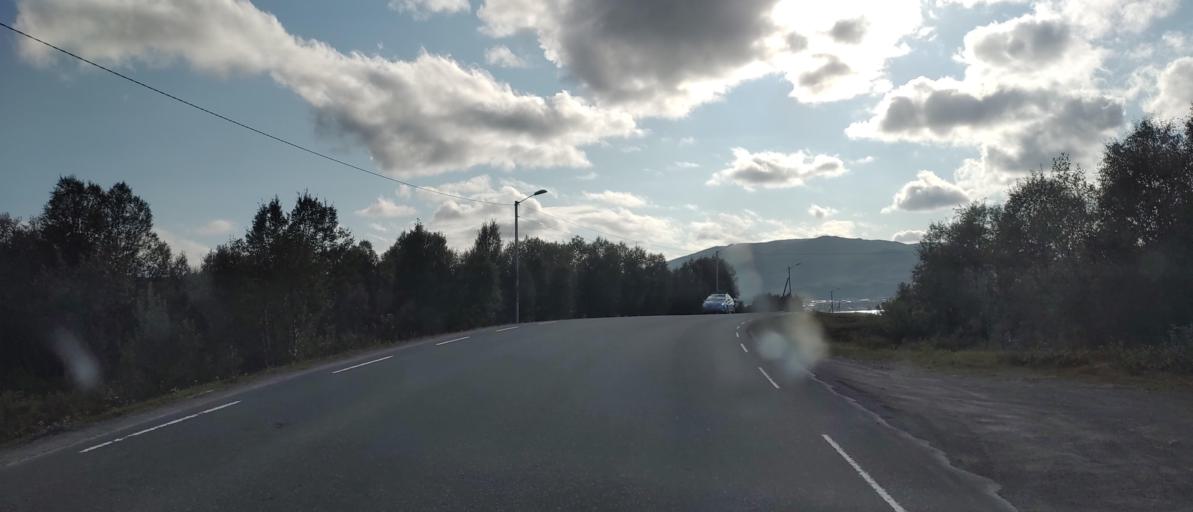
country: NO
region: Nordland
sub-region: Sortland
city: Sortland
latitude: 68.7206
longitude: 15.4636
